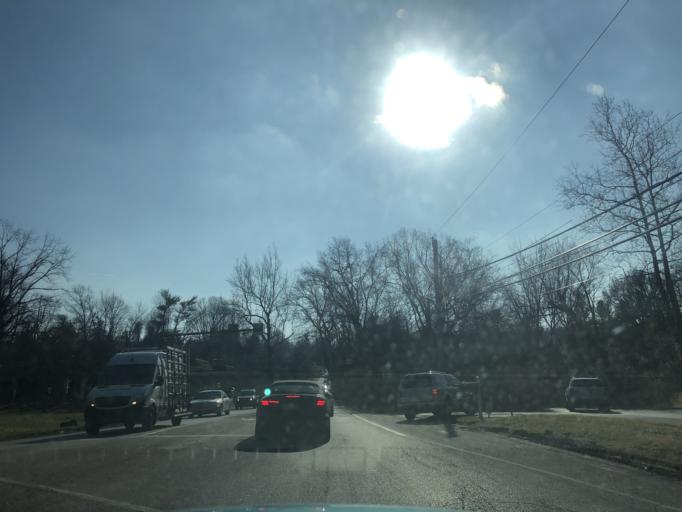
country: US
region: Pennsylvania
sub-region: Delaware County
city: Radnor
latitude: 40.0617
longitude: -75.3408
